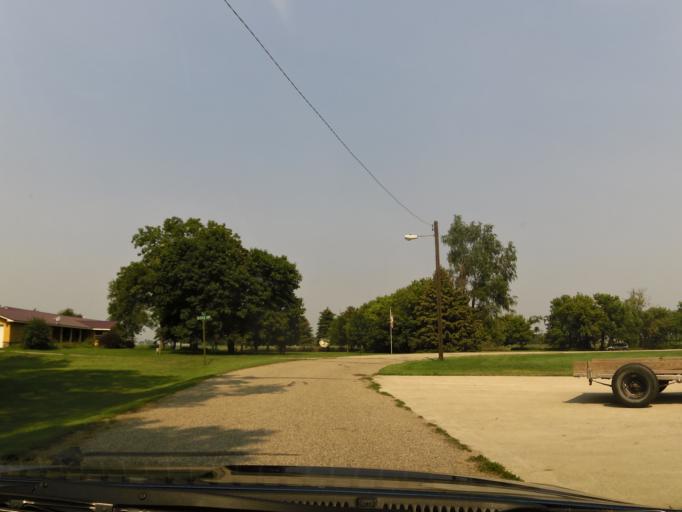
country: US
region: South Dakota
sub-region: Roberts County
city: Sisseton
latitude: 45.8575
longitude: -97.1058
